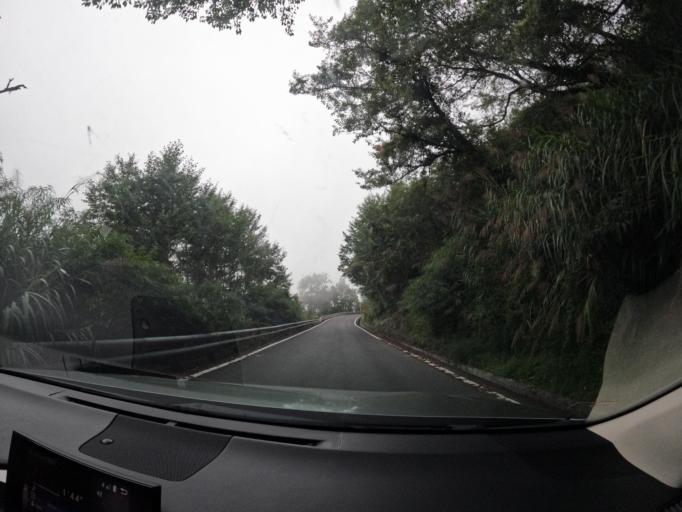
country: TW
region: Taiwan
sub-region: Taitung
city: Taitung
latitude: 23.2419
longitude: 120.9870
